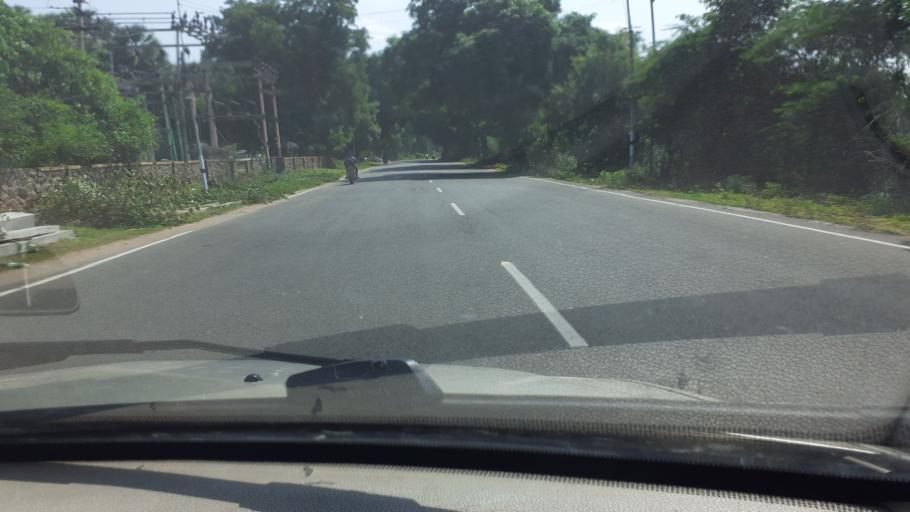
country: IN
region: Tamil Nadu
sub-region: Thoothukkudi
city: Srivaikuntam
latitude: 8.6312
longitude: 77.9030
